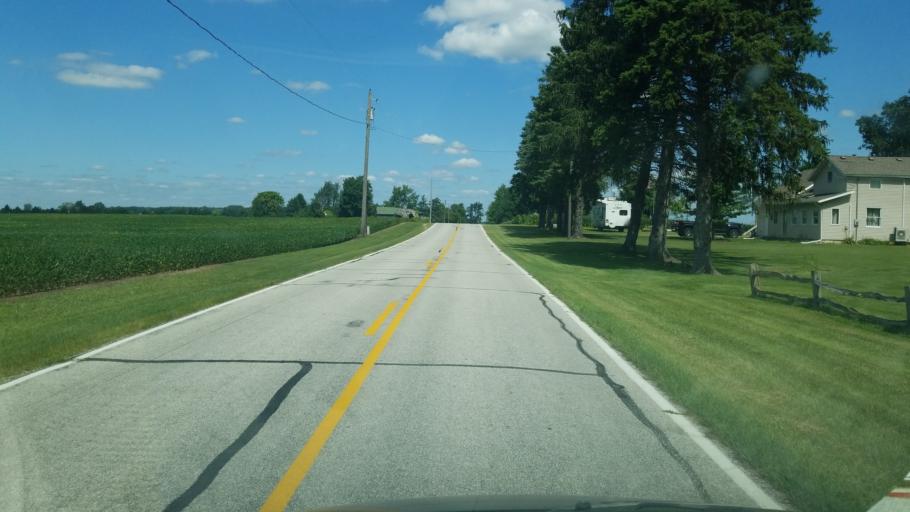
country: US
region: Ohio
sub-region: Fulton County
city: Delta
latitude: 41.6336
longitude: -84.0154
